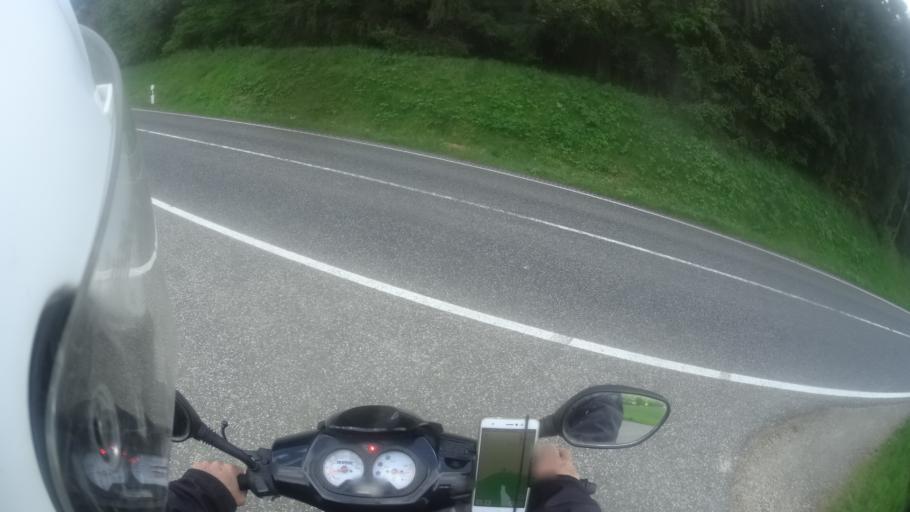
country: DE
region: Hesse
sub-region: Regierungsbezirk Darmstadt
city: Schlangenbad
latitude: 50.0821
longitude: 8.0338
